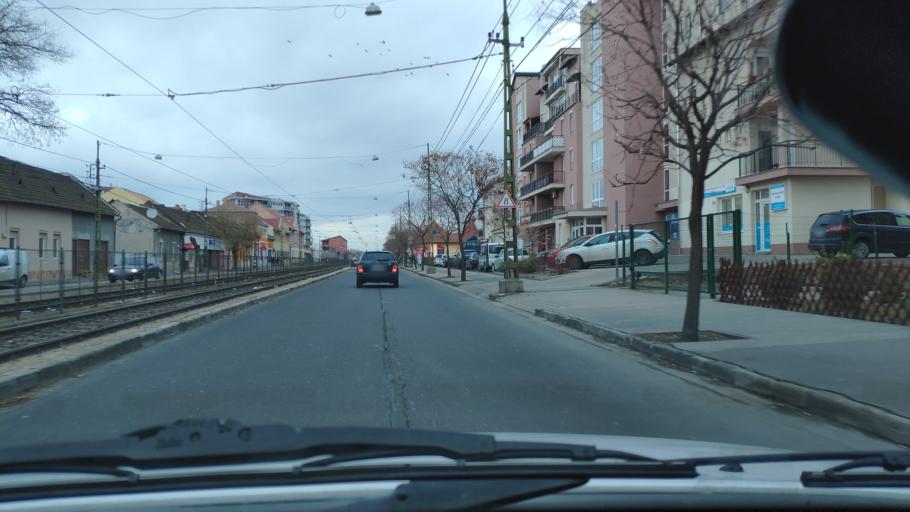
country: HU
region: Budapest
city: Budapest XXI. keruelet
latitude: 47.4250
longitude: 19.0673
